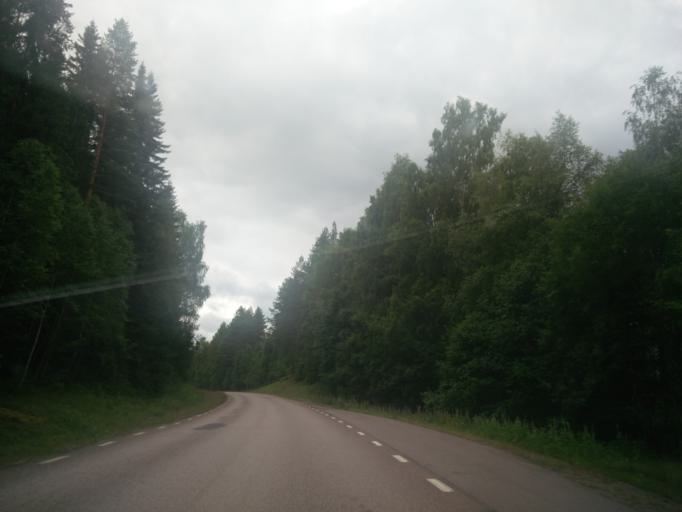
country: SE
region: Vaermland
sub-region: Arvika Kommun
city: Arvika
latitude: 59.9232
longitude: 12.6546
